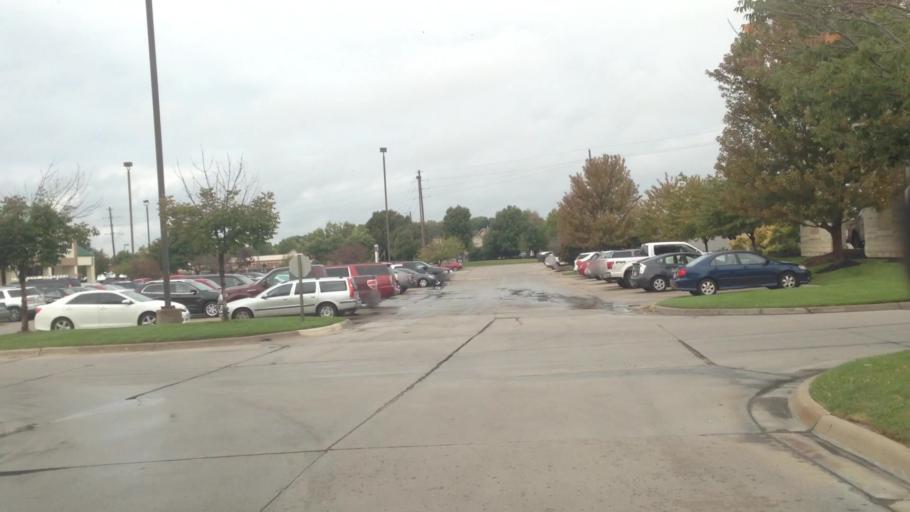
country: US
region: Kansas
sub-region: Douglas County
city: Lawrence
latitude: 38.9706
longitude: -95.3051
